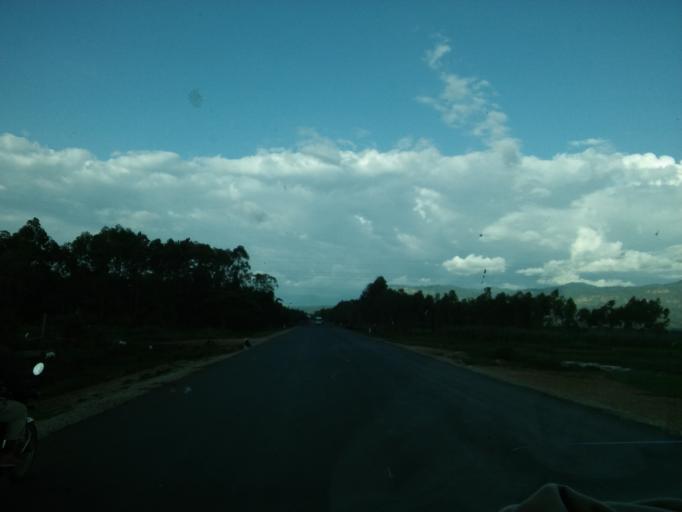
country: UG
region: Eastern Region
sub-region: Mbale District
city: Mbale
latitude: 1.0751
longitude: 34.1290
